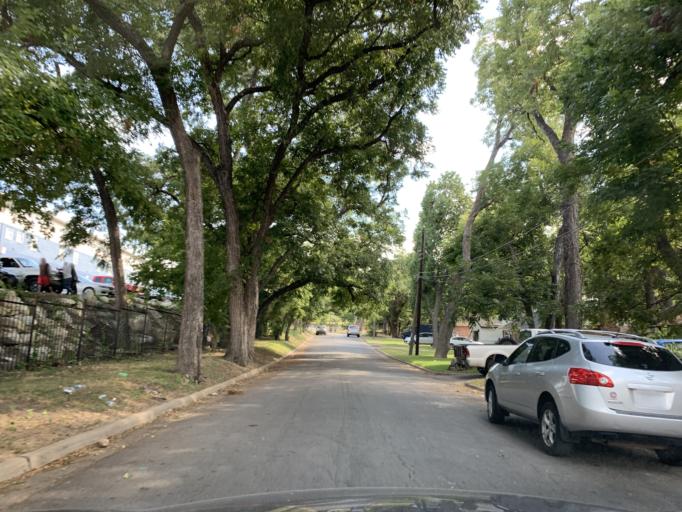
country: US
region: Texas
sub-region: Dallas County
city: Cockrell Hill
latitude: 32.7483
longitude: -96.8650
